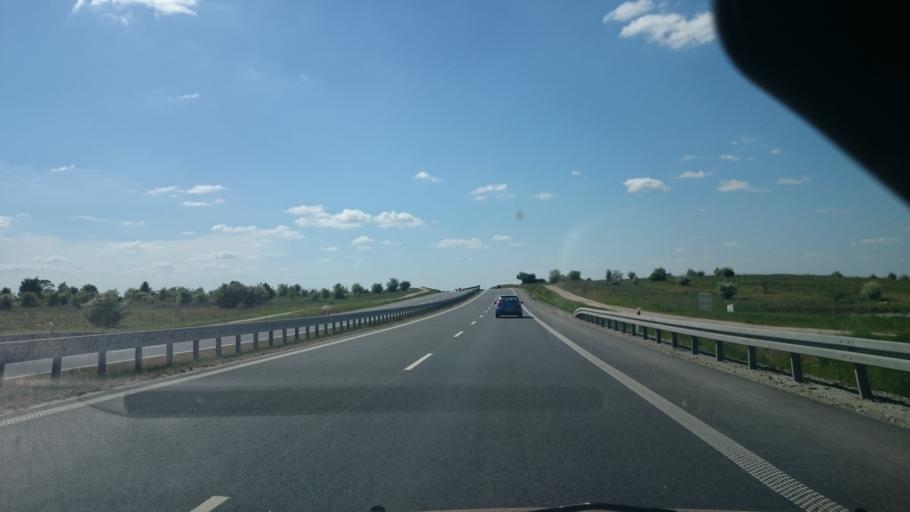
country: PL
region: Opole Voivodeship
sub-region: Powiat nyski
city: Nysa
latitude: 50.5007
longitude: 17.3124
